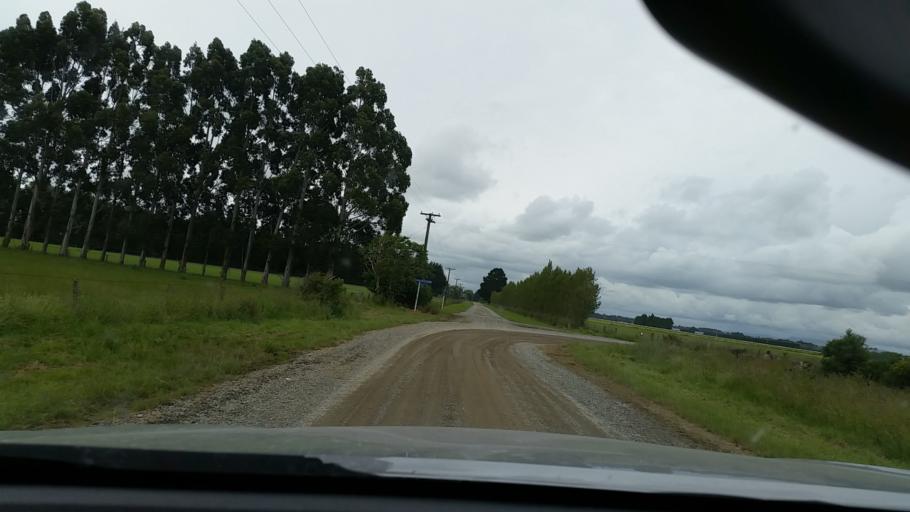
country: NZ
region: Southland
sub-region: Southland District
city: Winton
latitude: -46.1844
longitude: 168.2818
